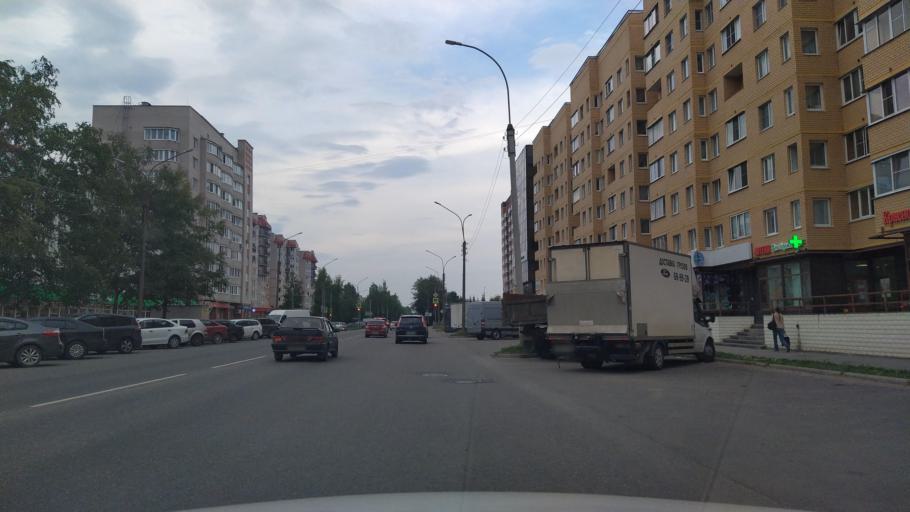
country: RU
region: Novgorod
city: Velikiy Novgorod
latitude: 58.5154
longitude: 31.2449
